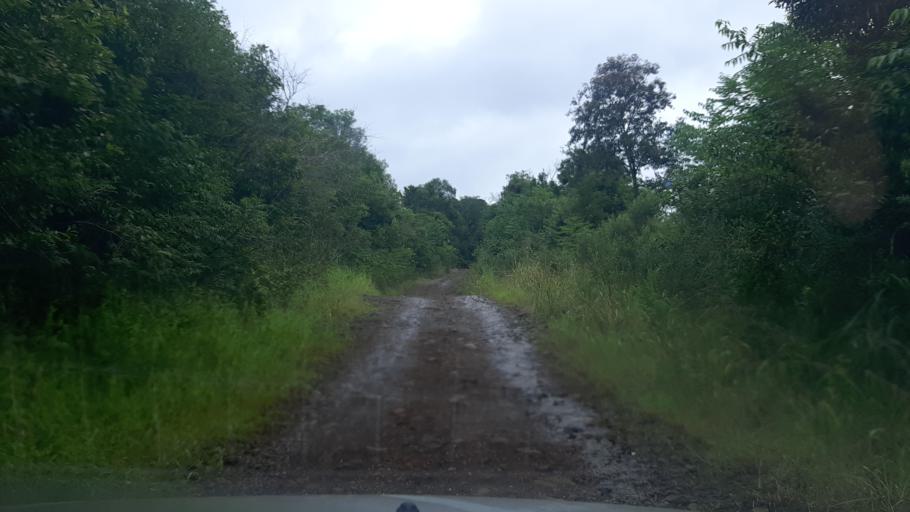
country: BR
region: Parana
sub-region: Ampere
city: Ampere
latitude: -26.0486
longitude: -53.5205
